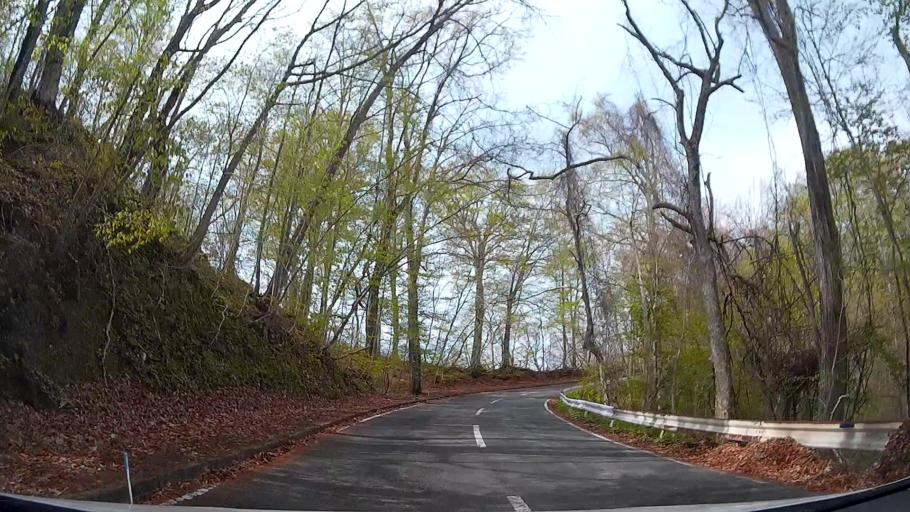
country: JP
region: Akita
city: Hanawa
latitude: 40.4378
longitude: 140.9167
